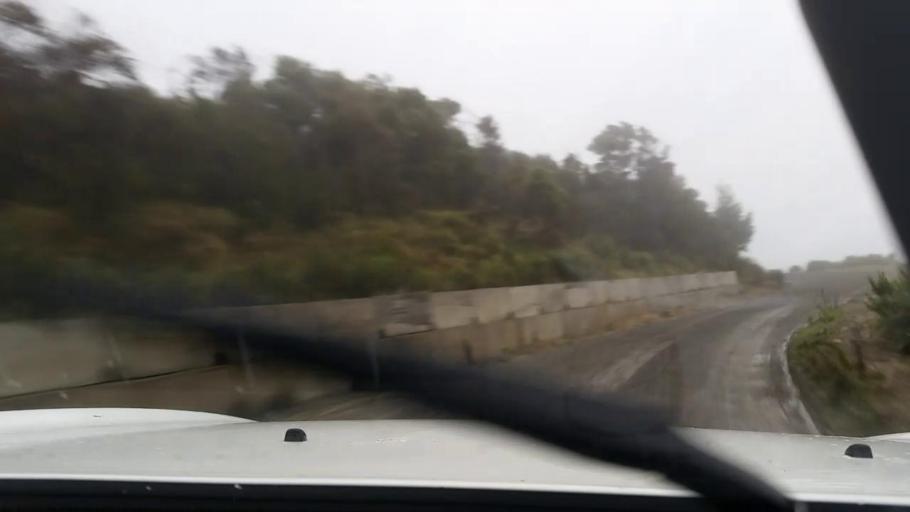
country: NZ
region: Wellington
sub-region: Masterton District
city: Masterton
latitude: -41.2448
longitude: 175.8776
